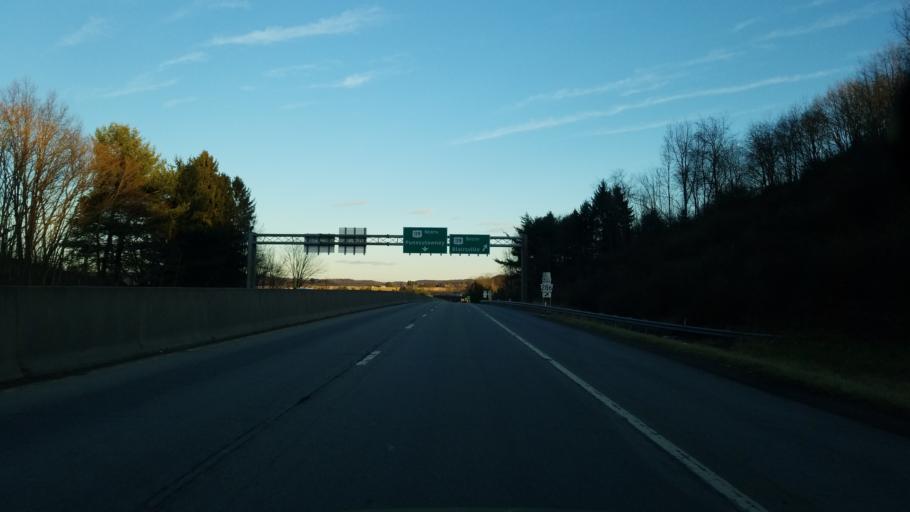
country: US
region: Pennsylvania
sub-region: Indiana County
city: Chevy Chase Heights
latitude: 40.6264
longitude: -79.1240
